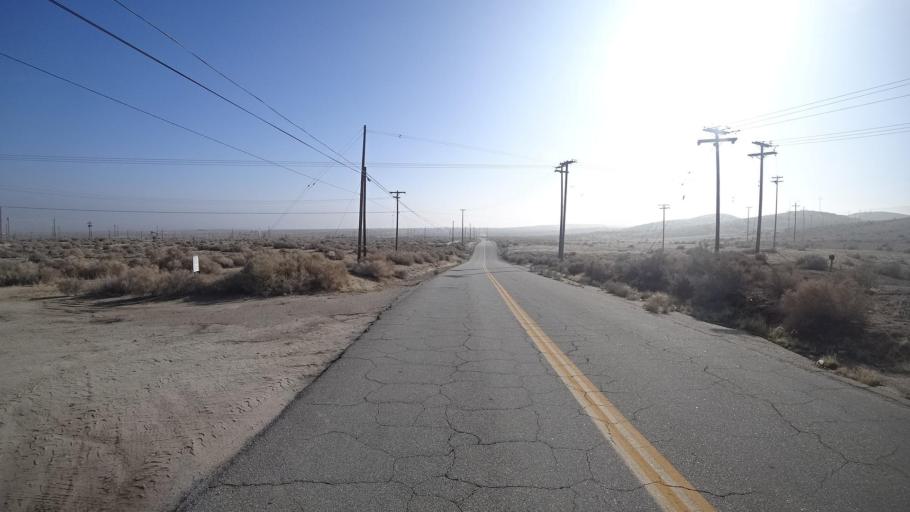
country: US
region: California
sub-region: Kern County
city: Taft Heights
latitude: 35.1937
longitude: -119.5809
